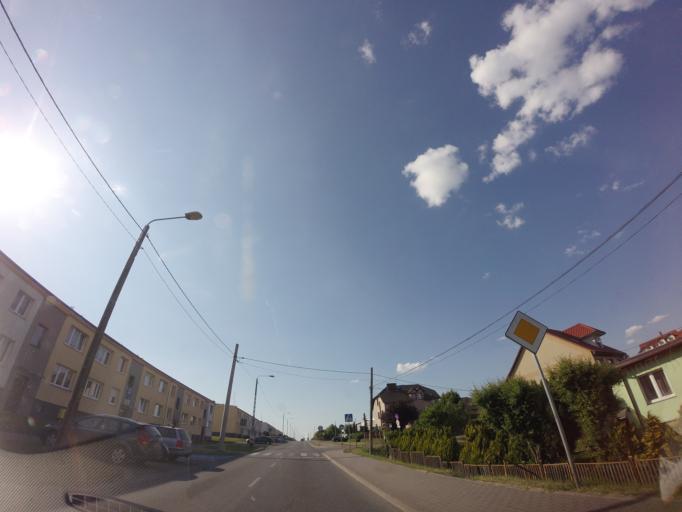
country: PL
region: West Pomeranian Voivodeship
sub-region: Powiat mysliborski
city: Barlinek
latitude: 52.9974
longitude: 15.2028
